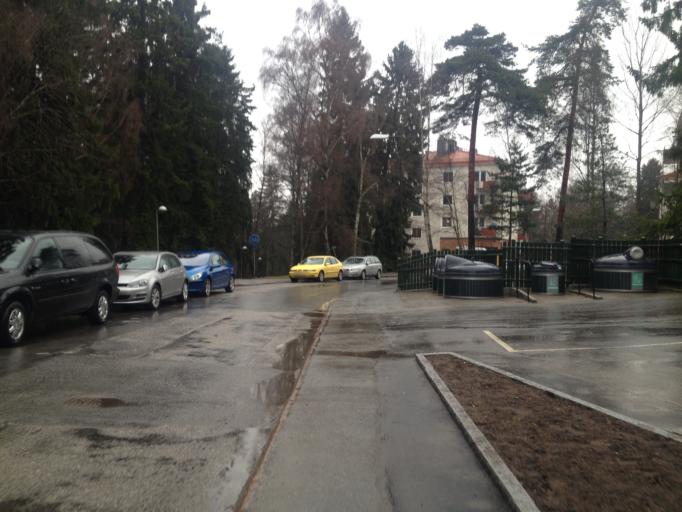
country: SE
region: Stockholm
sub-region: Stockholms Kommun
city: Arsta
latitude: 59.2751
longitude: 18.0659
